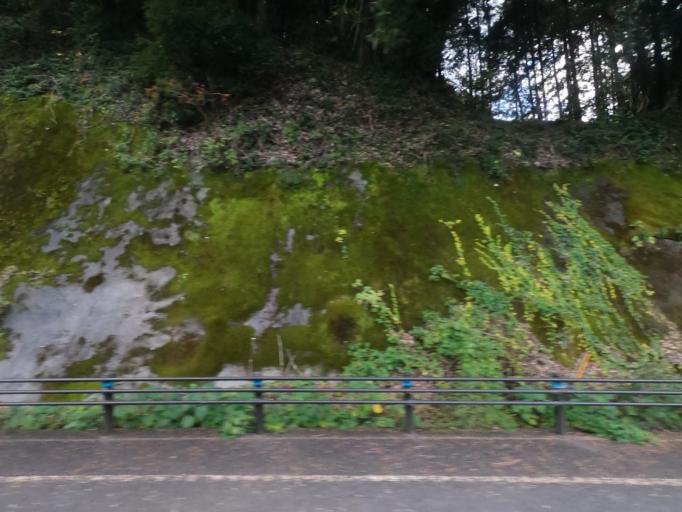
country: JP
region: Kumamoto
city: Minamata
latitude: 32.2611
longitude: 130.5087
